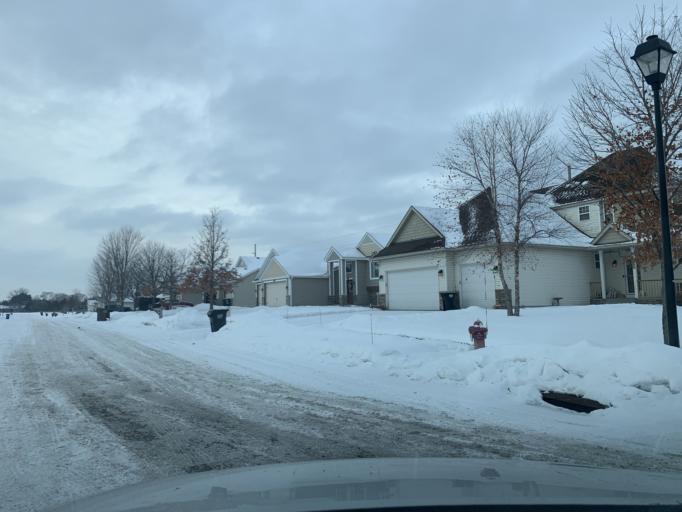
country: US
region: Minnesota
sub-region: Anoka County
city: Ramsey
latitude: 45.2479
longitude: -93.4109
